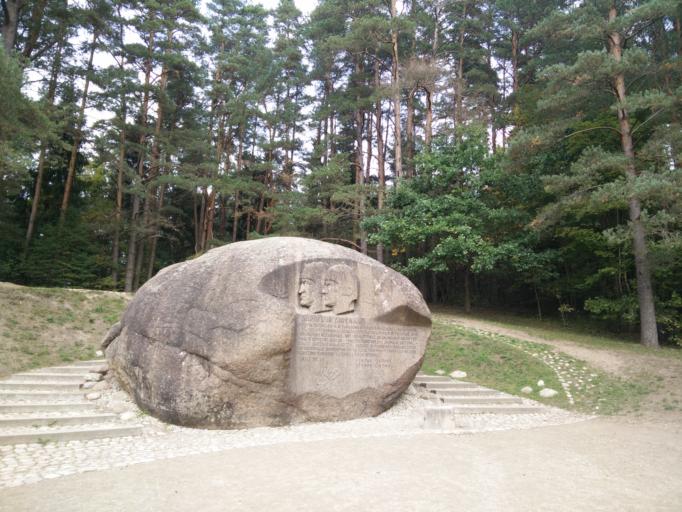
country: LT
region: Utenos apskritis
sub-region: Anyksciai
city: Anyksciai
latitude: 55.4841
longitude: 25.0597
